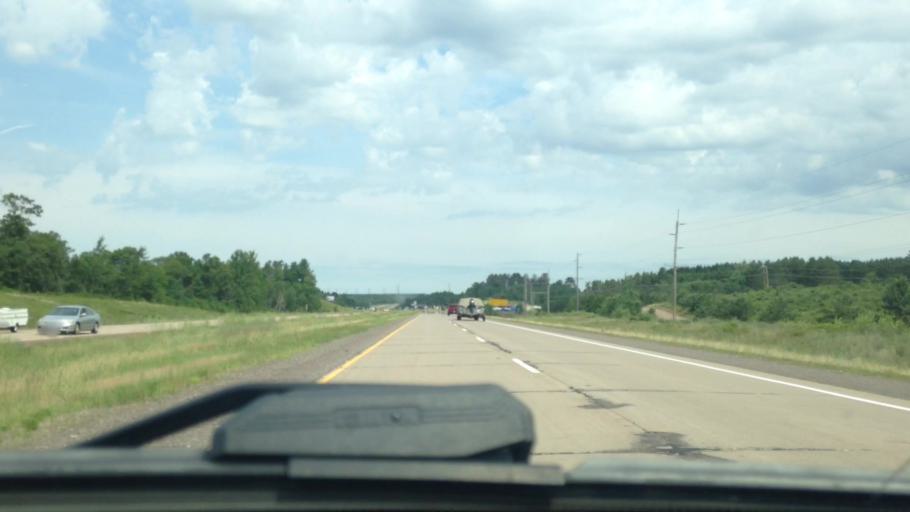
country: US
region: Wisconsin
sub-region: Douglas County
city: Lake Nebagamon
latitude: 46.2343
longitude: -91.8003
